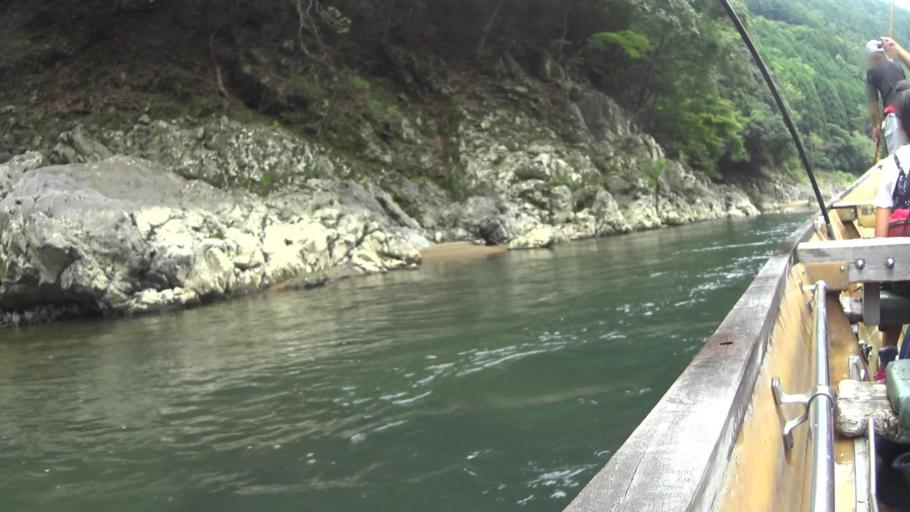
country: JP
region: Kyoto
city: Kameoka
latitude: 35.0228
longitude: 135.6319
